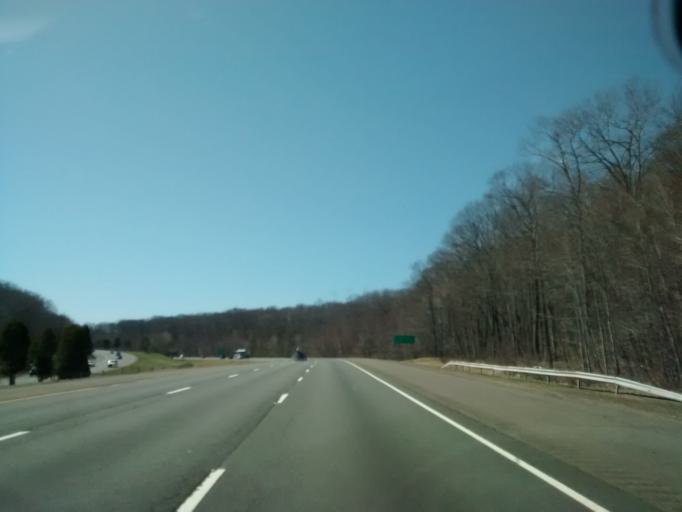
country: US
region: Connecticut
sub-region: Tolland County
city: Tolland
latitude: 41.8552
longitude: -72.3953
